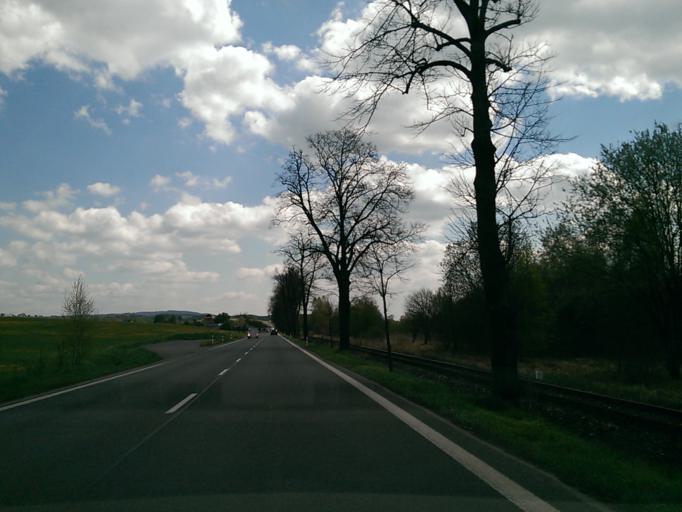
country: CZ
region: Liberecky
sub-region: Okres Semily
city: Turnov
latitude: 50.5659
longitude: 15.1880
